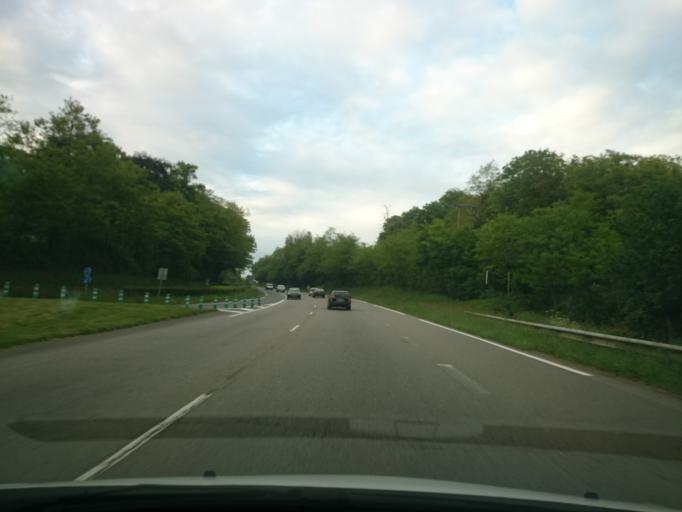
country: FR
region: Pays de la Loire
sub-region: Departement de la Loire-Atlantique
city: Saint-Herblain
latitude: 47.2442
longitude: -1.6356
